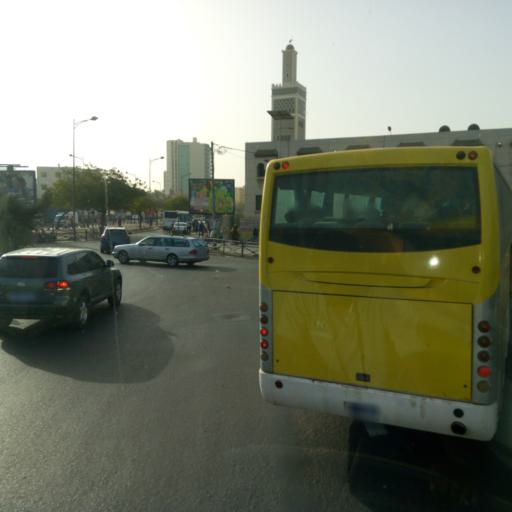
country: SN
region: Dakar
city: Dakar
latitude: 14.6795
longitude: -17.4431
